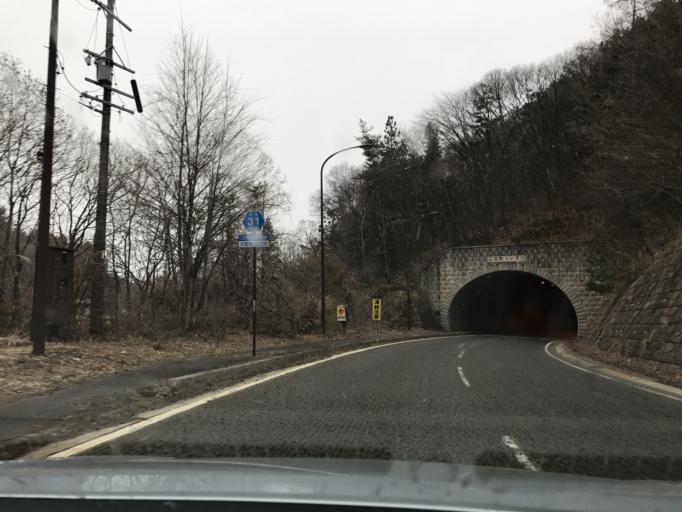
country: JP
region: Nagano
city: Omachi
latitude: 36.5253
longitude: 137.8658
